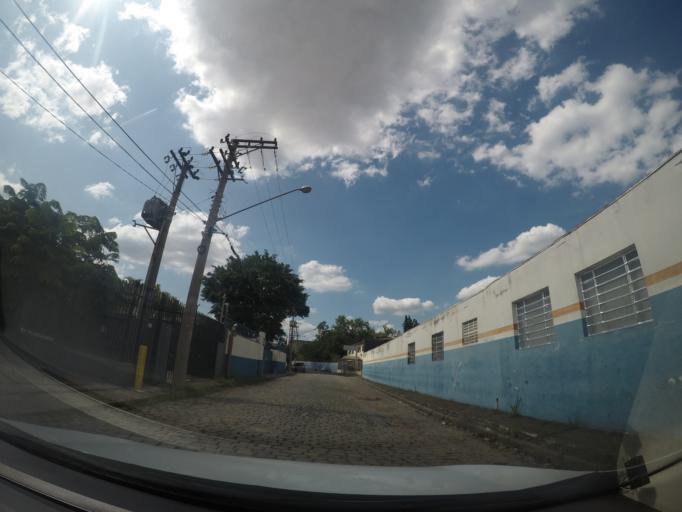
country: BR
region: Sao Paulo
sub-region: Guarulhos
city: Guarulhos
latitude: -23.4721
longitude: -46.5133
